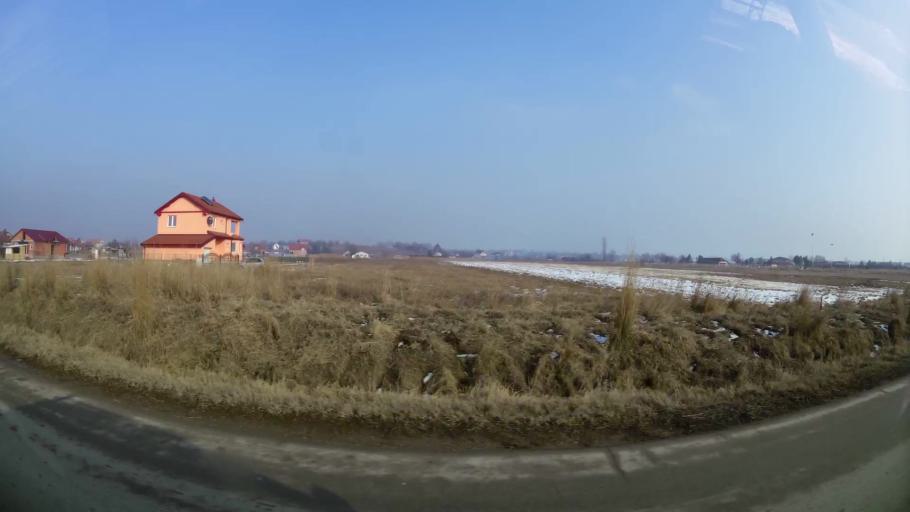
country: MK
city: Kadino
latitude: 41.9779
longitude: 21.5935
